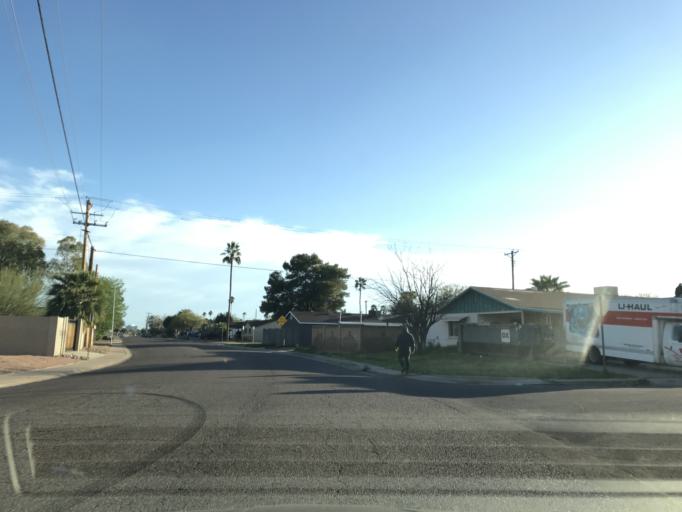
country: US
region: Arizona
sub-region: Maricopa County
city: Tempe Junction
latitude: 33.4644
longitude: -111.9306
